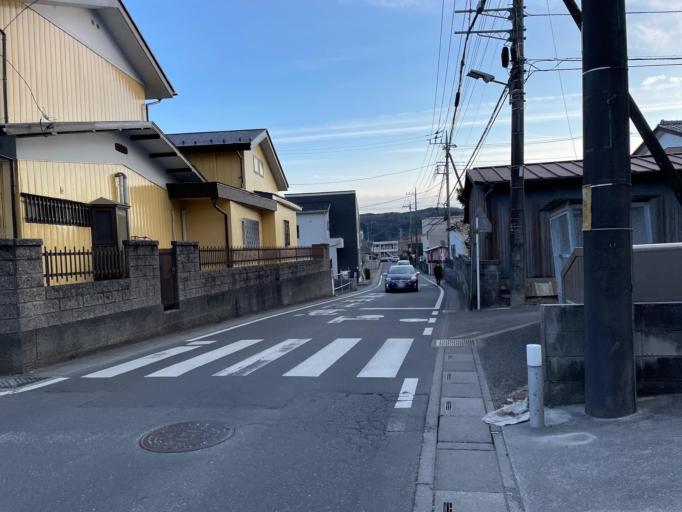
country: JP
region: Saitama
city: Hanno
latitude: 35.8425
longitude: 139.3476
